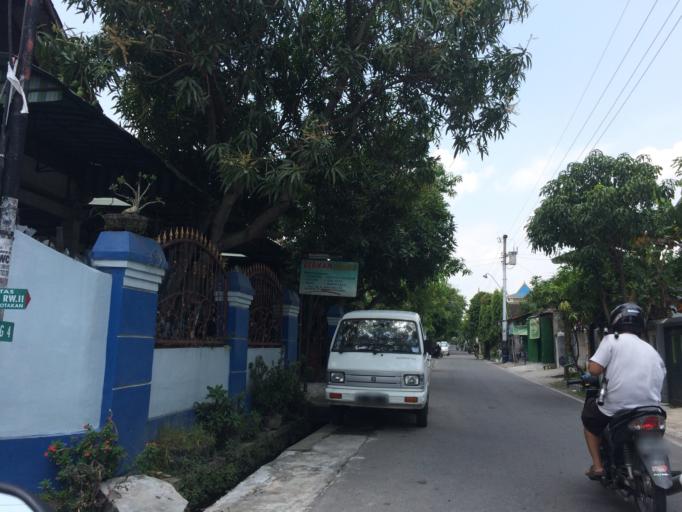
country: ID
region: Central Java
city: Grogol
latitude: -7.5927
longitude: 110.8197
